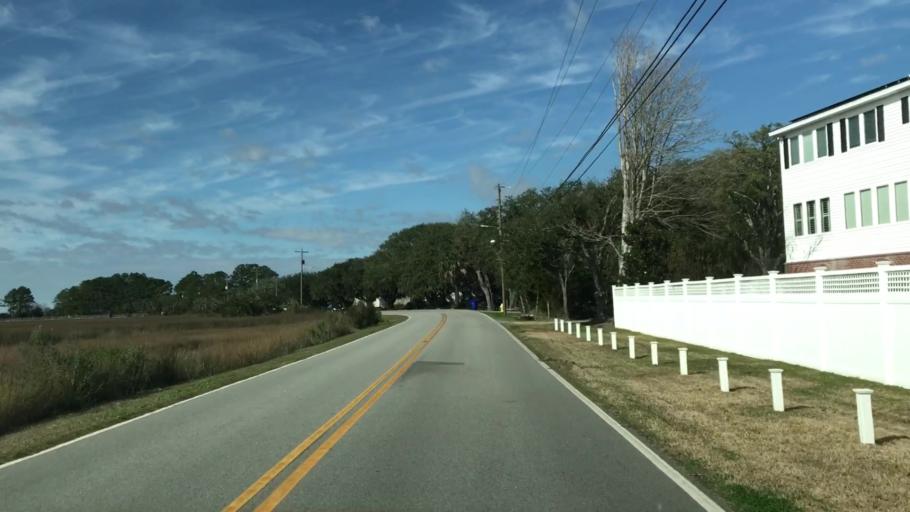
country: US
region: South Carolina
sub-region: Charleston County
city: Charleston
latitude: 32.7732
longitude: -80.0107
